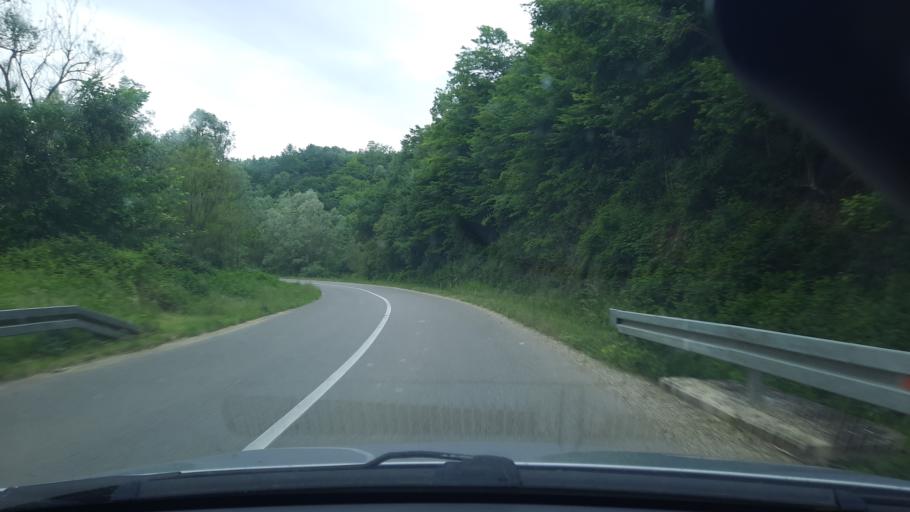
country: RS
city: Jarebice
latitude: 44.4990
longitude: 19.4855
